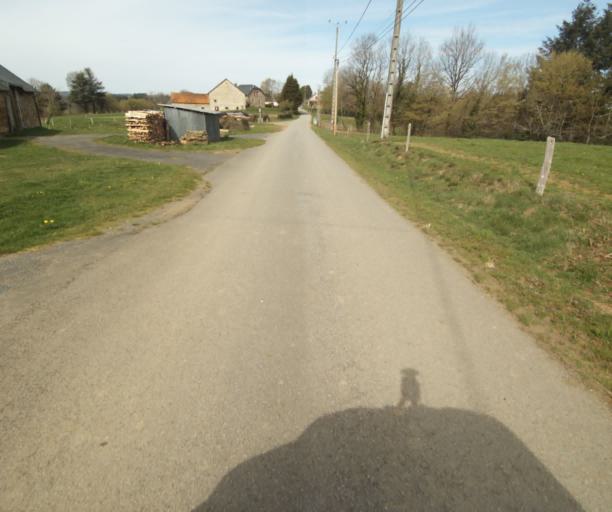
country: FR
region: Limousin
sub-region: Departement de la Correze
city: Correze
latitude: 45.3929
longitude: 1.8116
